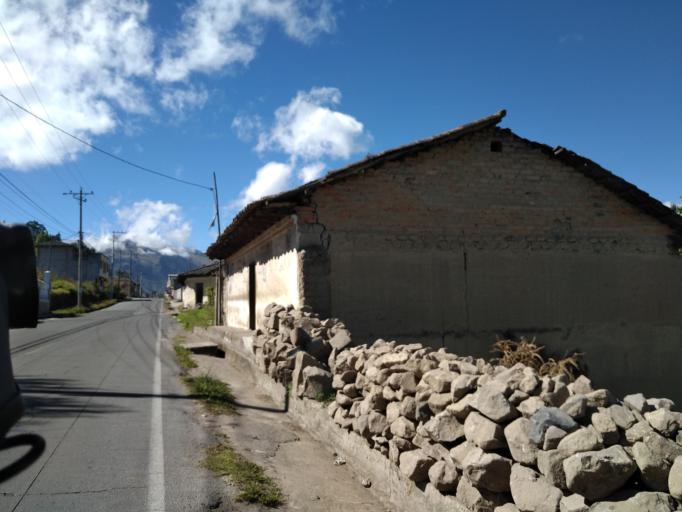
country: EC
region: Imbabura
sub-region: Canton Otavalo
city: Otavalo
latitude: 0.2140
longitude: -78.2128
